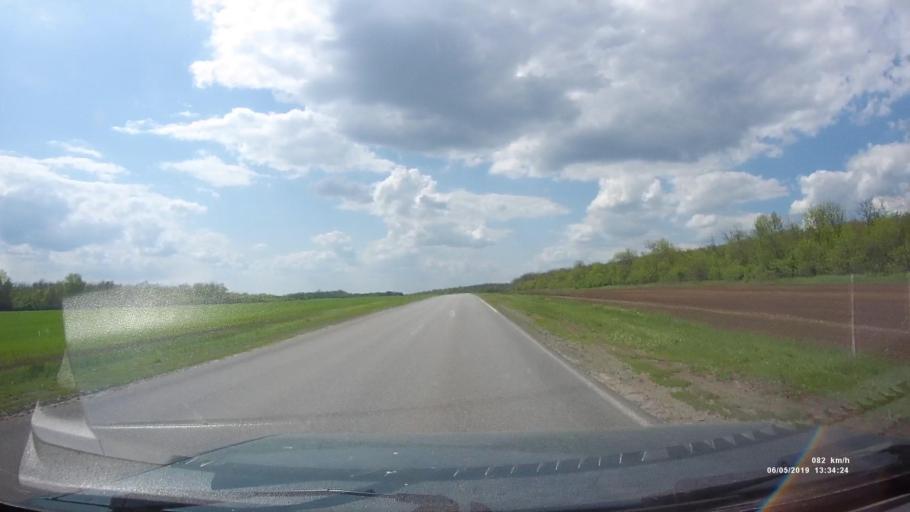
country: RU
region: Rostov
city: Ust'-Donetskiy
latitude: 47.6929
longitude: 40.7636
